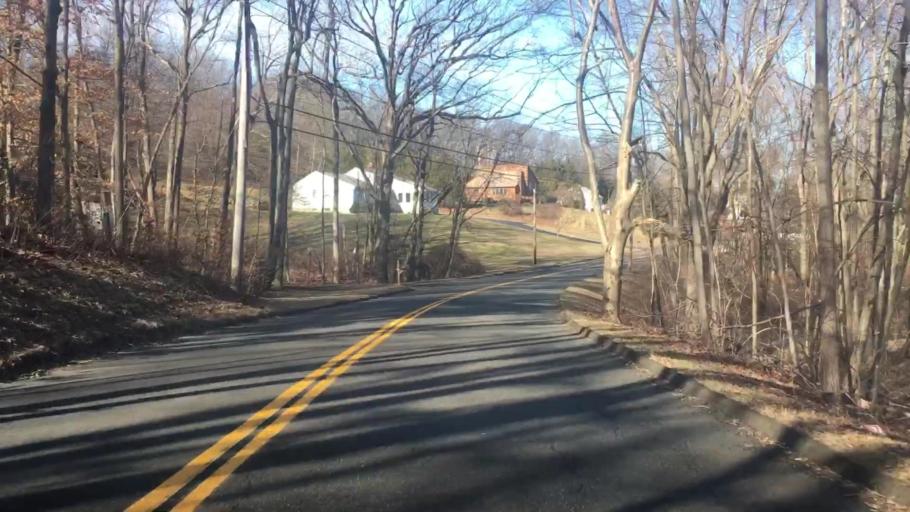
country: US
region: Connecticut
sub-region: Middlesex County
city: Durham
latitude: 41.5135
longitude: -72.6485
